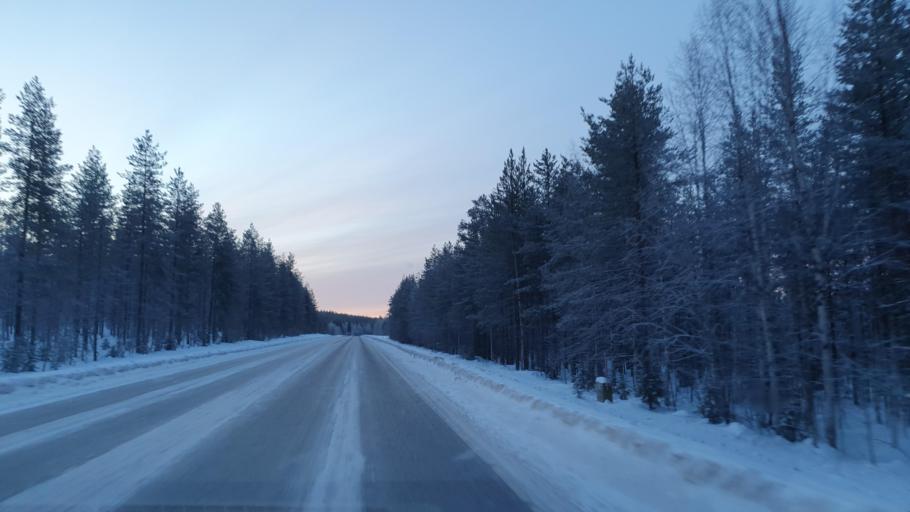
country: FI
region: Lapland
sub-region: Torniolaakso
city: Pello
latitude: 66.9426
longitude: 24.0729
